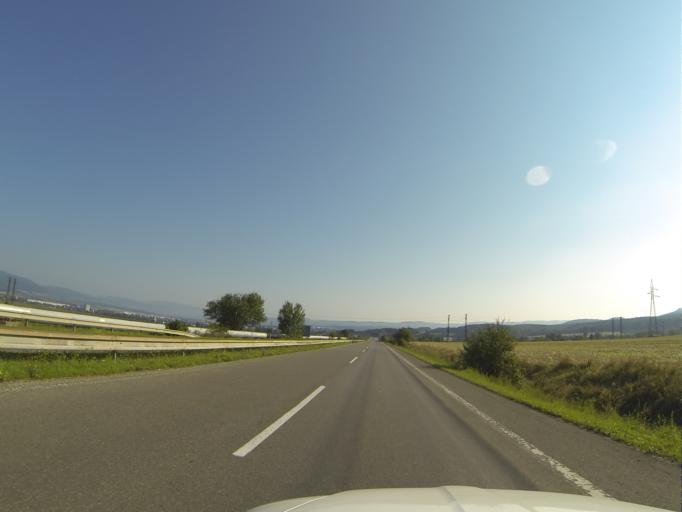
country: SK
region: Nitriansky
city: Prievidza
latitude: 48.7404
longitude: 18.6170
